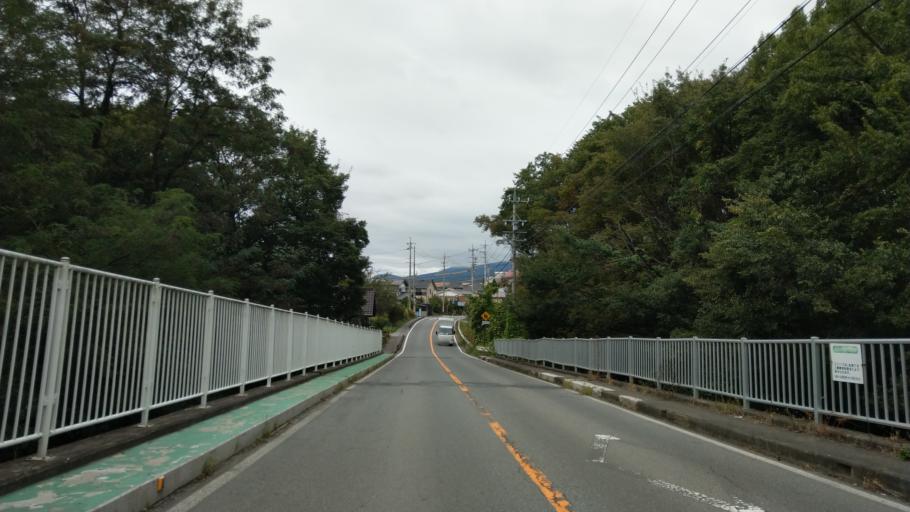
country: JP
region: Nagano
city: Komoro
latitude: 36.3188
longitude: 138.4286
